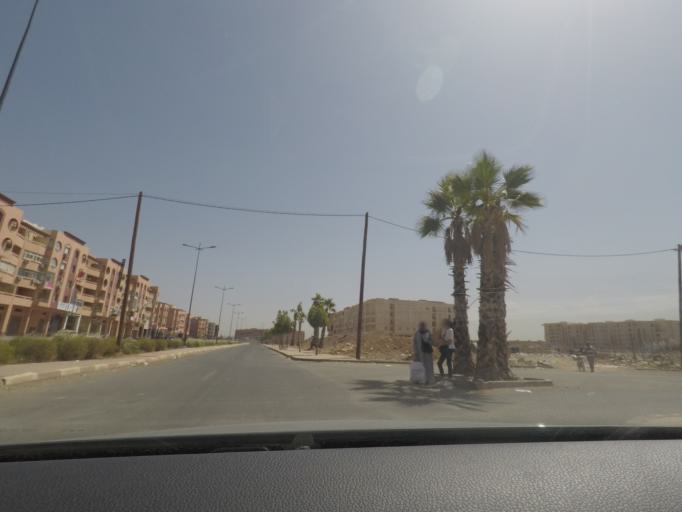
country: MA
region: Marrakech-Tensift-Al Haouz
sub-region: Marrakech
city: Marrakesh
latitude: 31.5877
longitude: -8.0391
